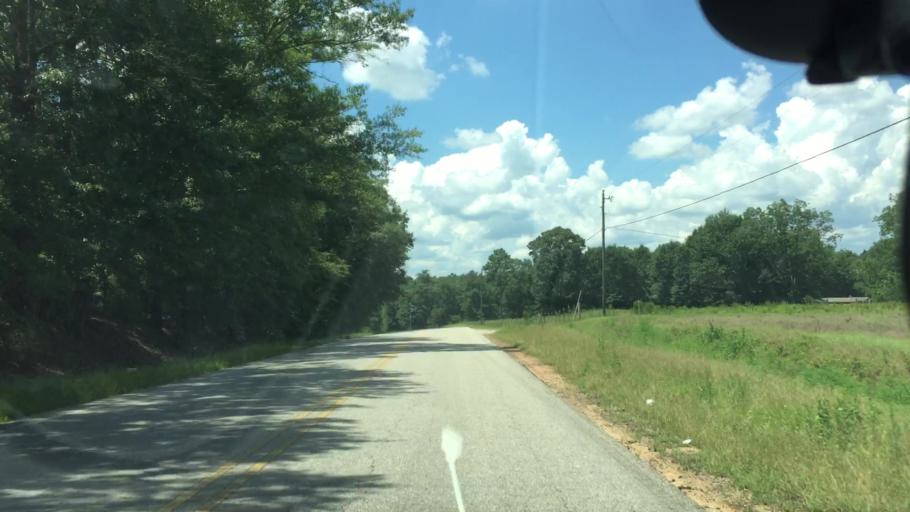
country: US
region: Alabama
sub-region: Pike County
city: Troy
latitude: 31.7486
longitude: -85.9754
